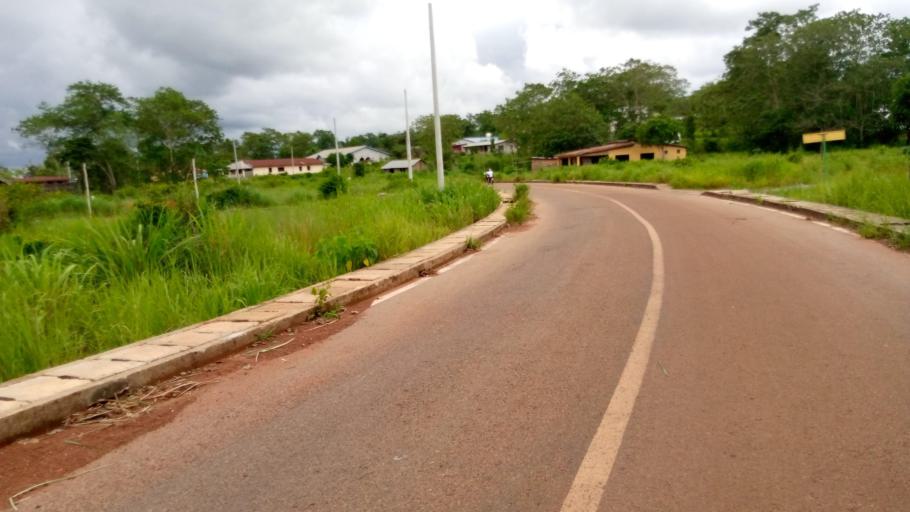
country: SL
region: Southern Province
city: Moyamba
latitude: 8.1615
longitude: -12.4495
